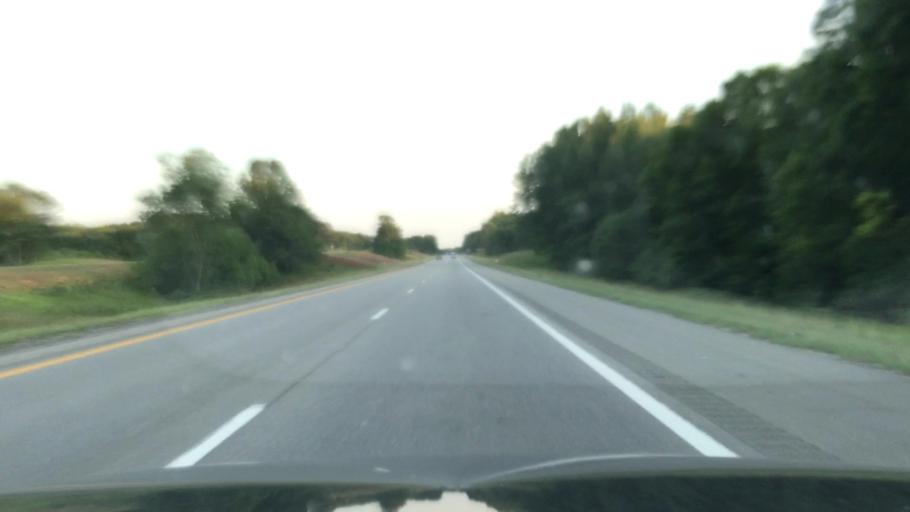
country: US
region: Michigan
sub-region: Montcalm County
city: Howard City
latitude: 43.5076
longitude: -85.4867
